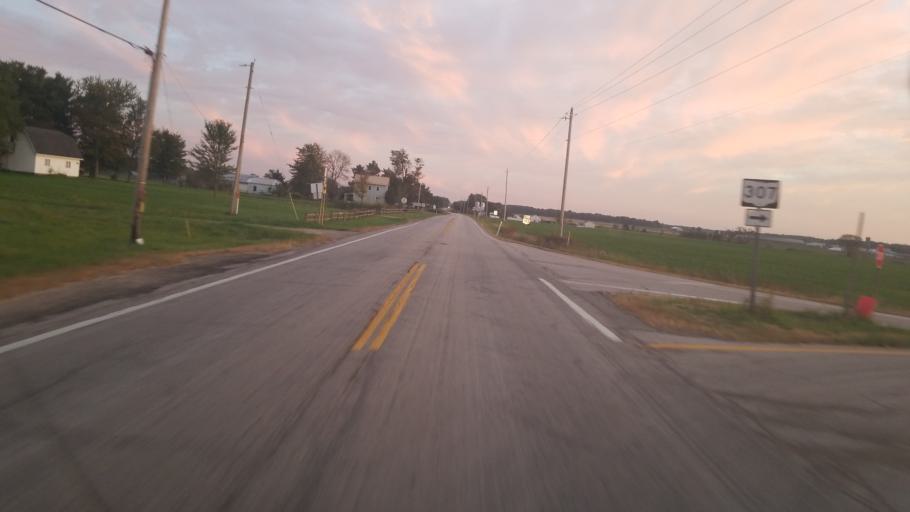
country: US
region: Ohio
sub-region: Ashtabula County
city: Andover
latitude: 41.6726
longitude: -80.6677
